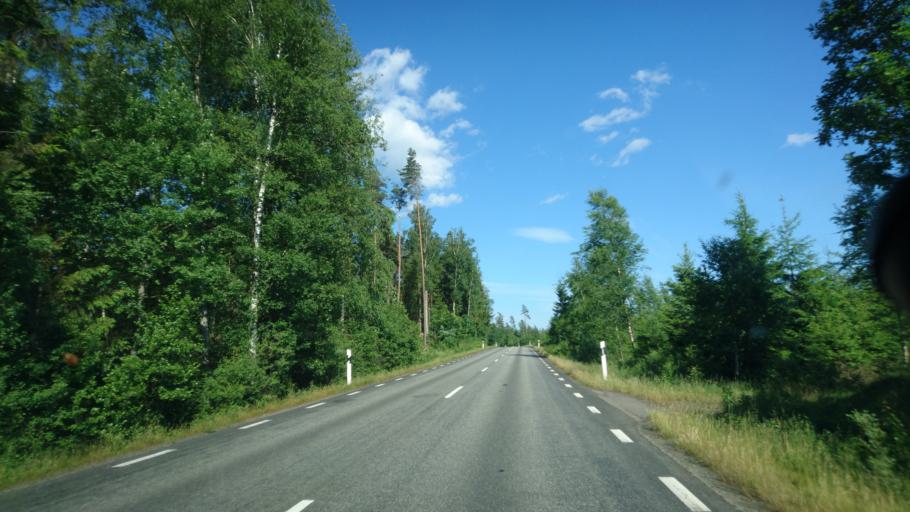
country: SE
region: Skane
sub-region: Osby Kommun
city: Lonsboda
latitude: 56.3899
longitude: 14.4041
